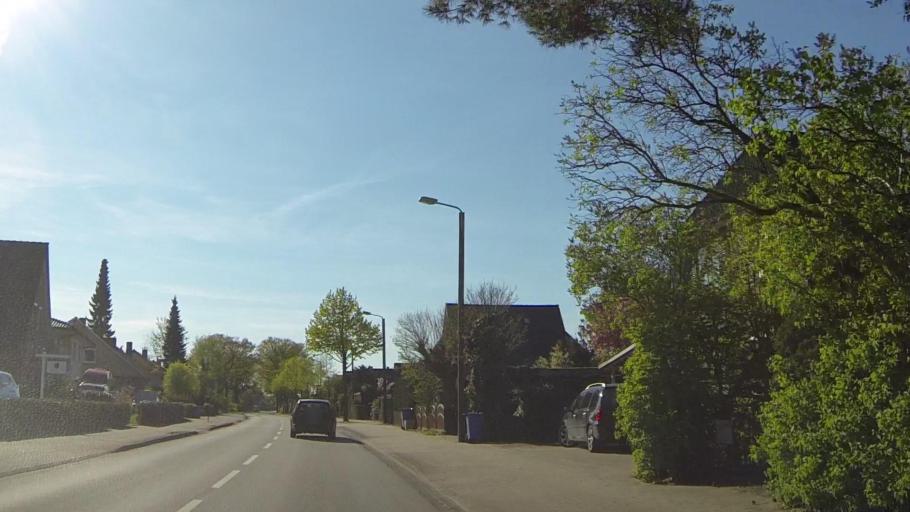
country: DE
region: Schleswig-Holstein
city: Pinneberg
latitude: 53.6485
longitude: 9.7867
